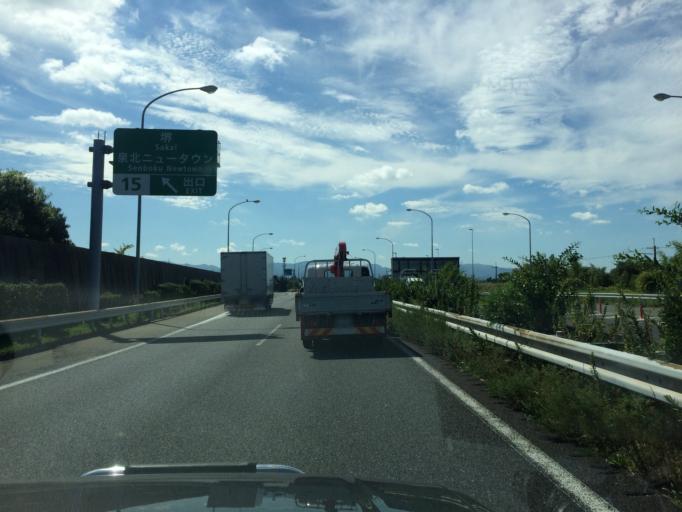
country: JP
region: Osaka
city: Takaishi
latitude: 34.5143
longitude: 135.4900
